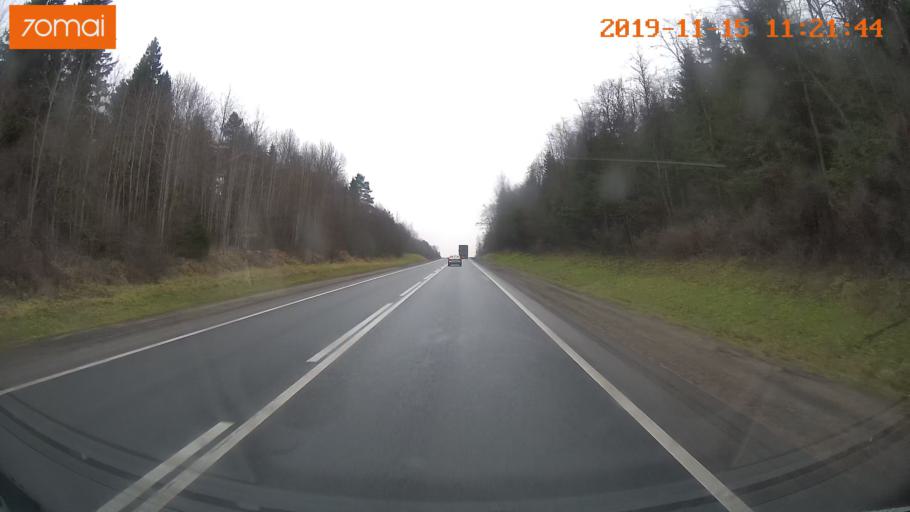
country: RU
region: Vologda
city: Molochnoye
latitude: 59.1455
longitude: 39.3453
